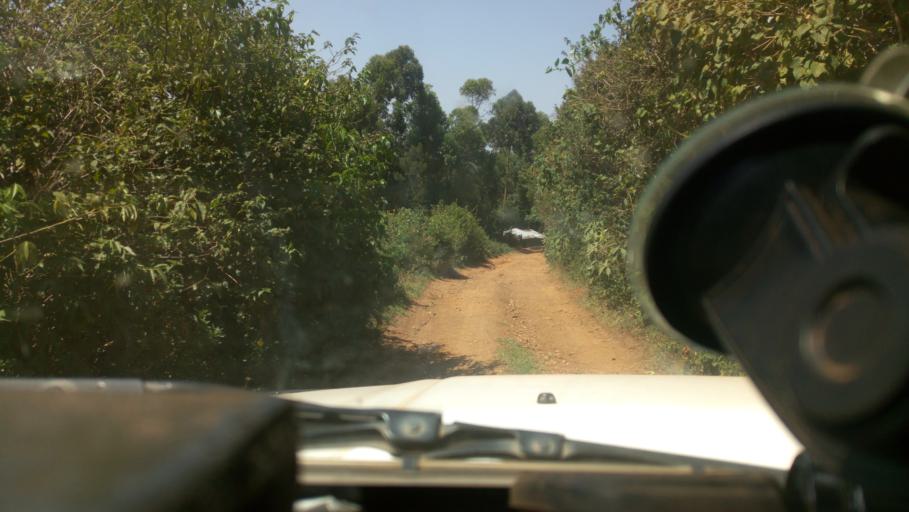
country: KE
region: Nyamira District
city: Keroka
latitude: -0.7328
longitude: 35.0175
